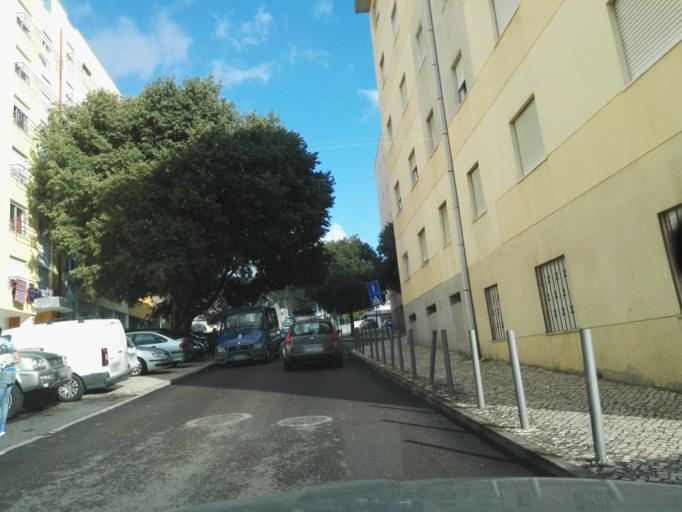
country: PT
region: Lisbon
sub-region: Amadora
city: Amadora
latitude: 38.7331
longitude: -9.2061
